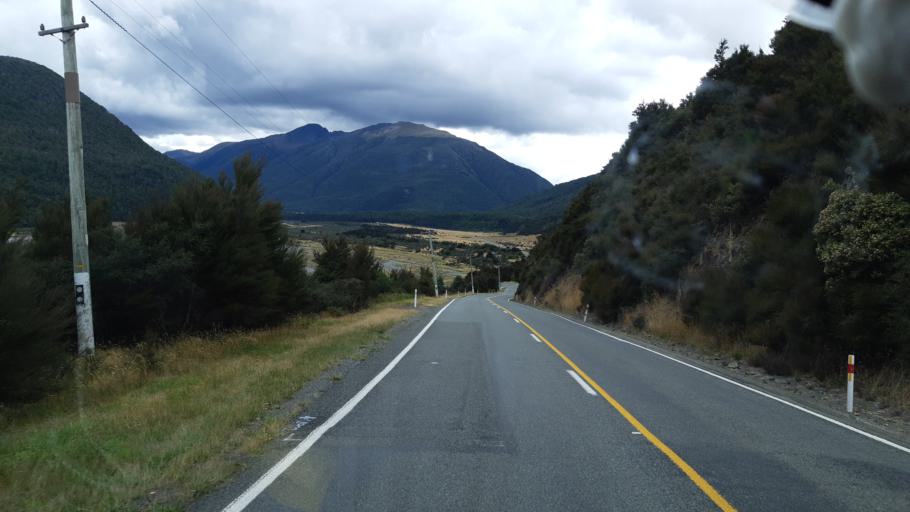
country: NZ
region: Canterbury
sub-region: Hurunui District
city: Amberley
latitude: -42.5436
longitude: 172.3569
